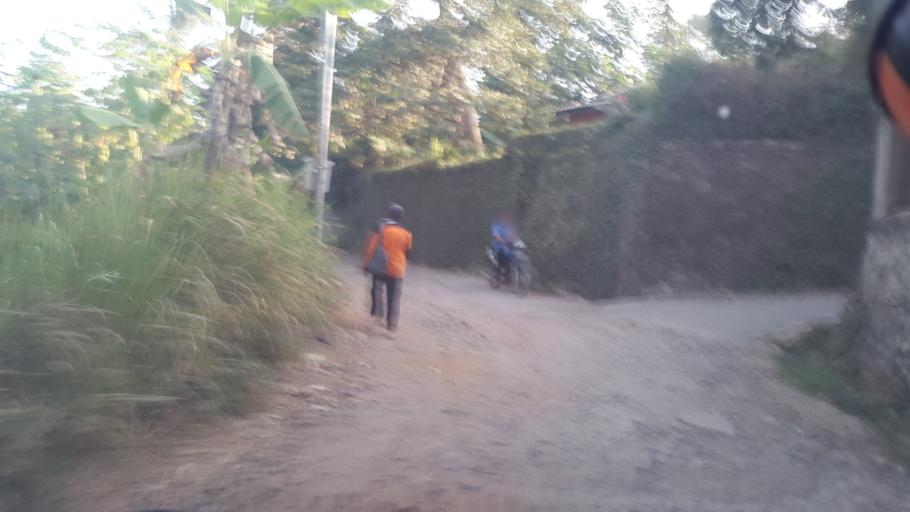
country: ID
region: West Java
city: Cicurug
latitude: -6.8161
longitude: 106.7518
